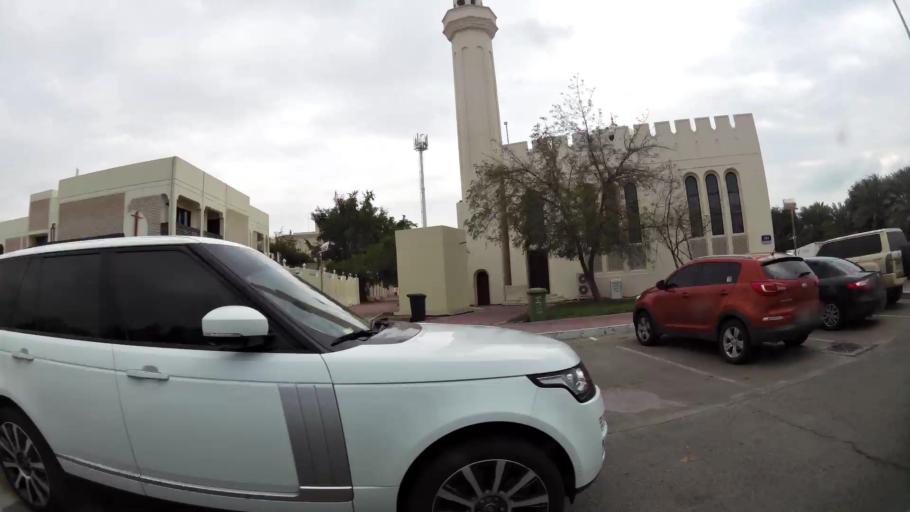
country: AE
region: Abu Dhabi
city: Abu Dhabi
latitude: 24.4337
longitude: 54.3839
